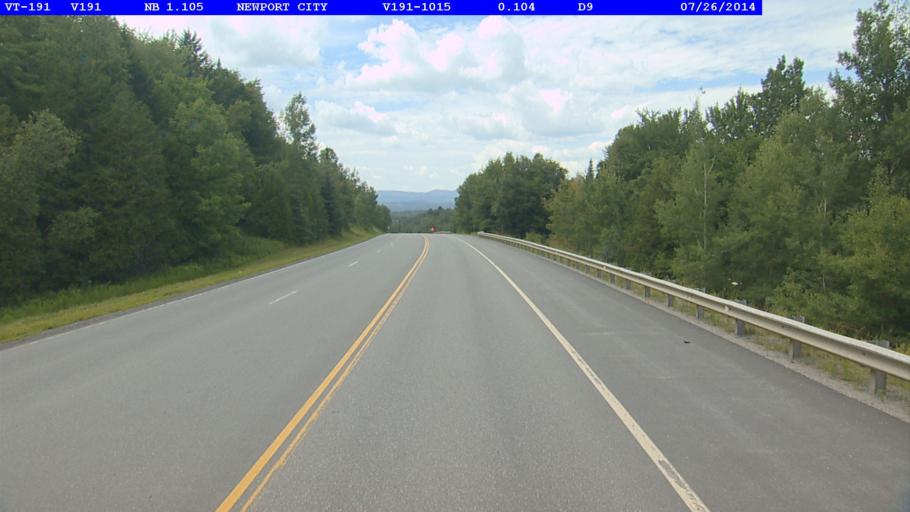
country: US
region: Vermont
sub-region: Orleans County
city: Newport
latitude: 44.9334
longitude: -72.1836
